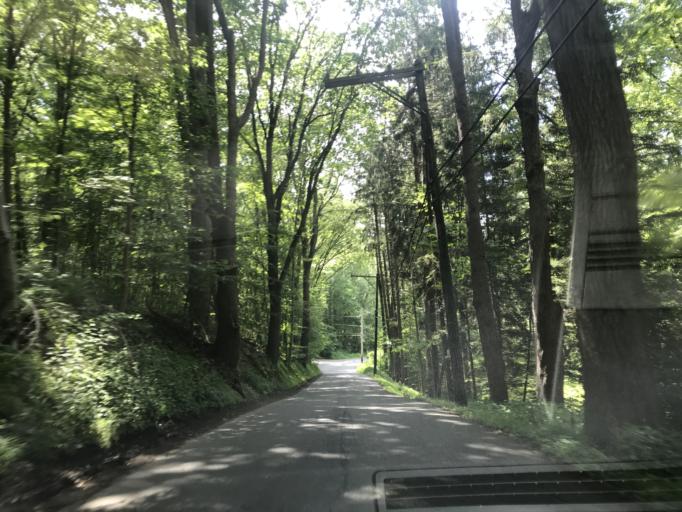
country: US
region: Delaware
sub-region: New Castle County
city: Greenville
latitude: 39.7838
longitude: -75.6454
